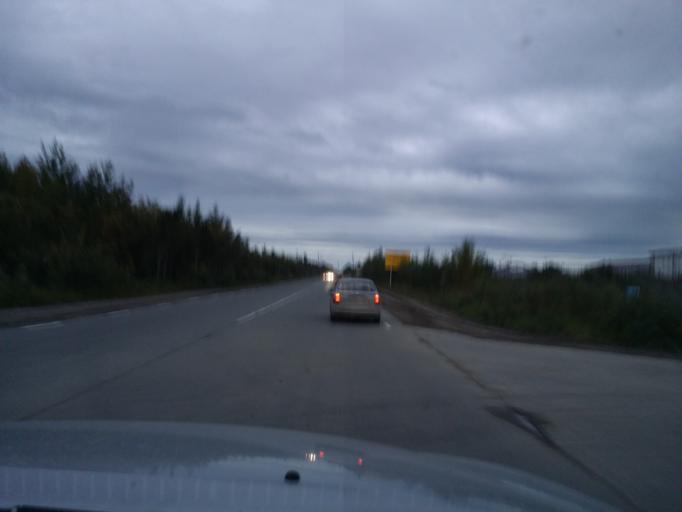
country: RU
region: Khanty-Mansiyskiy Avtonomnyy Okrug
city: Nizhnevartovsk
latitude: 60.9595
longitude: 76.6628
